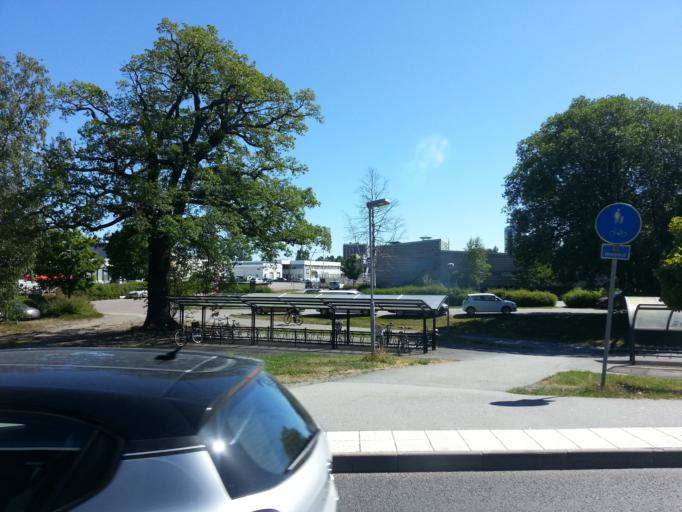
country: SE
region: Stockholm
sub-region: Tyreso Kommun
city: Bollmora
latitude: 59.2443
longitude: 18.2146
